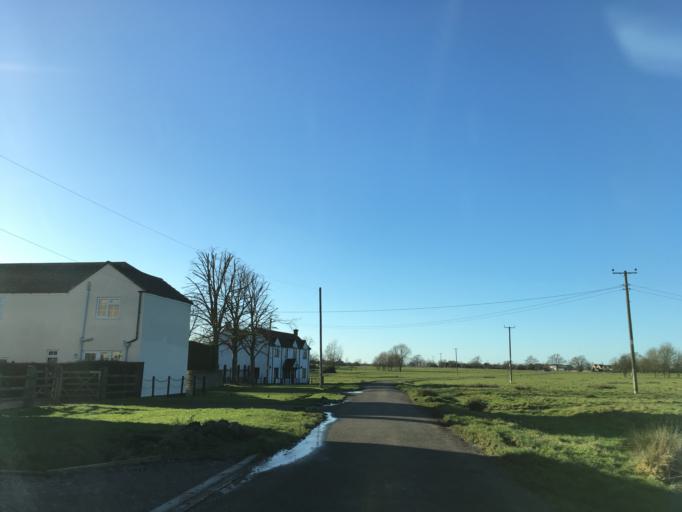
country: GB
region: England
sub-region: South Gloucestershire
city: Horton
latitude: 51.5525
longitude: -2.3695
